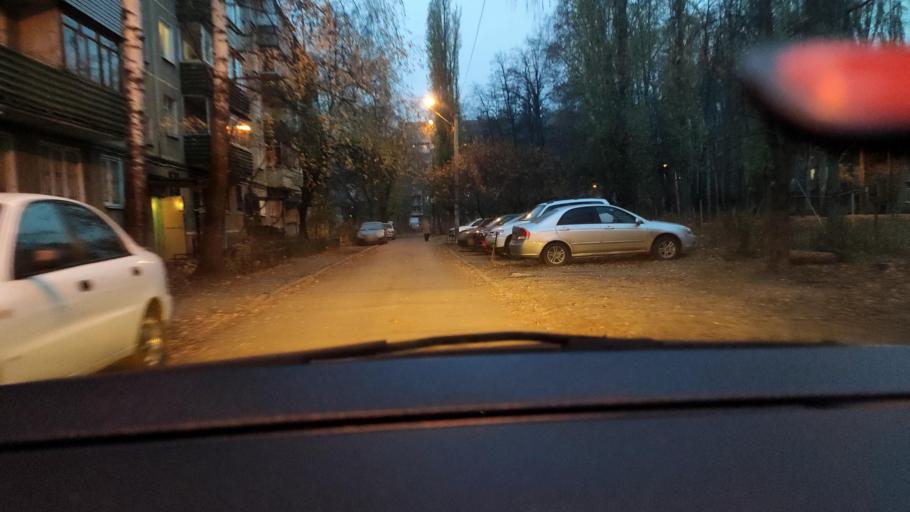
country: RU
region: Voronezj
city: Voronezh
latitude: 51.7005
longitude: 39.1898
